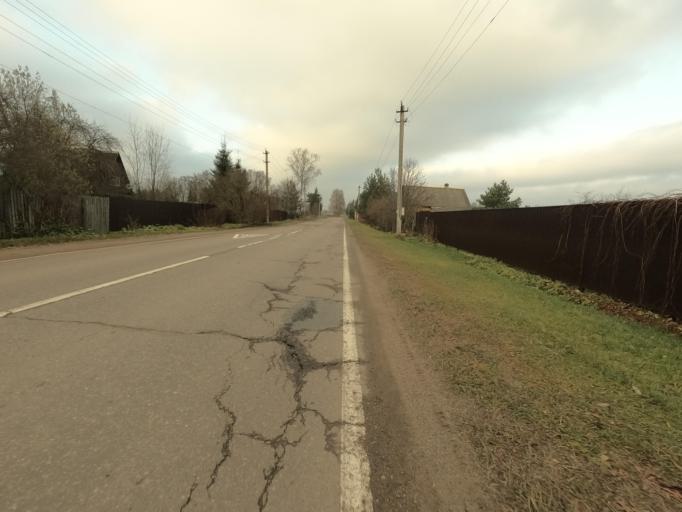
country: RU
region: Leningrad
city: Mga
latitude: 59.7750
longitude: 31.0243
